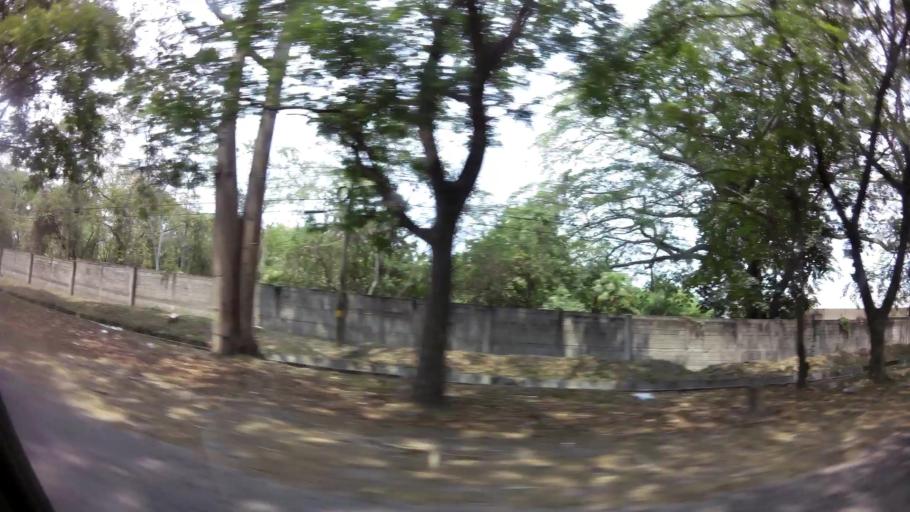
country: HN
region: Cortes
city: Villanueva
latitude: 15.3556
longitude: -87.9856
